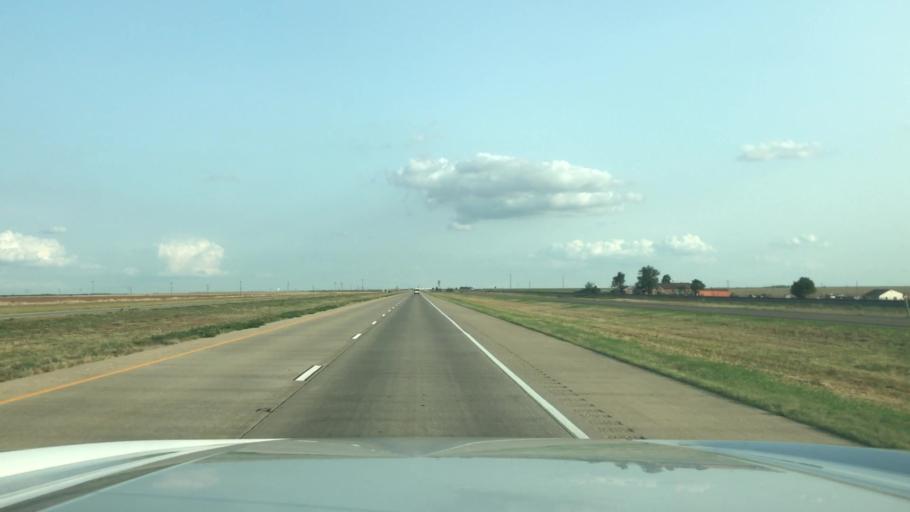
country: US
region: Texas
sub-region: Swisher County
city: Tulia
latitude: 34.6230
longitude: -101.8155
